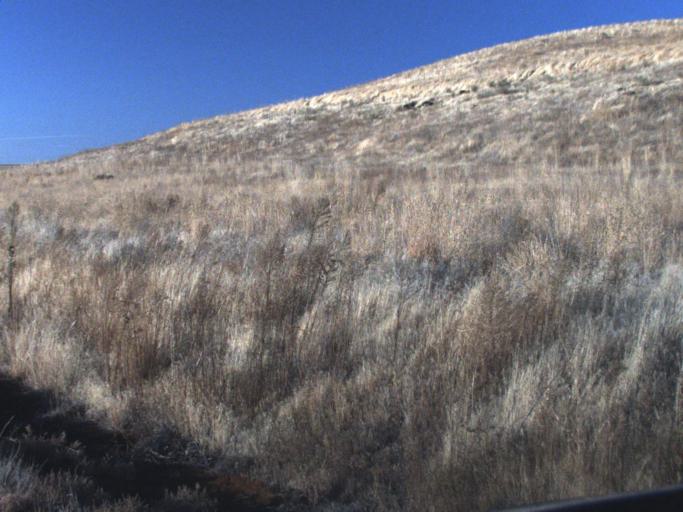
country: US
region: Washington
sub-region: Adams County
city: Ritzville
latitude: 46.6822
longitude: -118.3825
